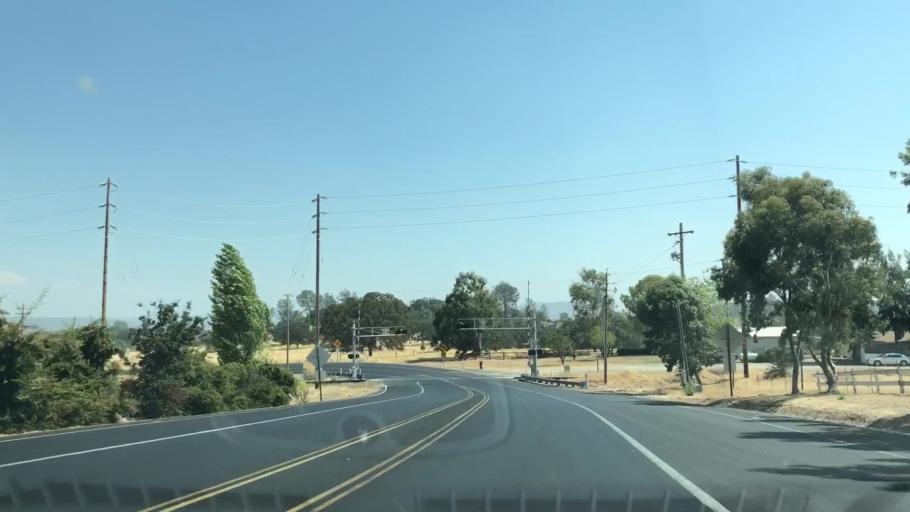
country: US
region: California
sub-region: Tuolumne County
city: Jamestown
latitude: 37.8784
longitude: -120.4611
